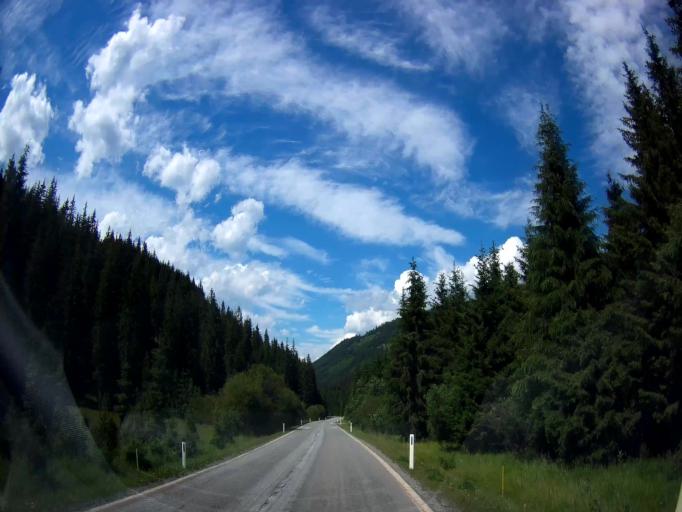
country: AT
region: Styria
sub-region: Politischer Bezirk Murau
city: Stadl an der Mur
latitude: 46.9943
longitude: 14.0151
